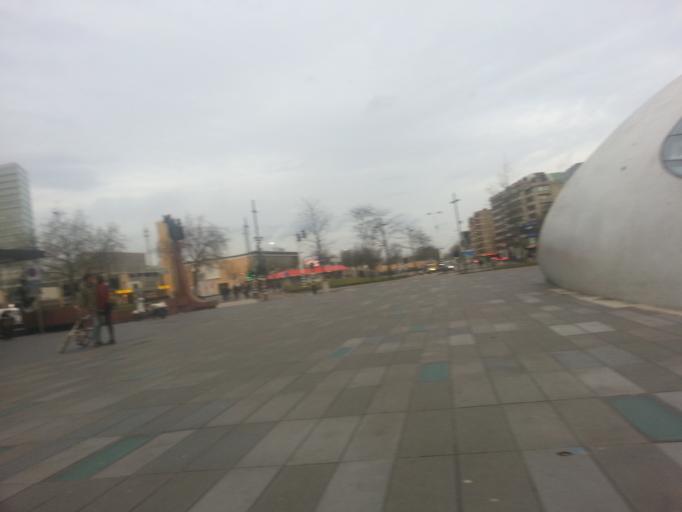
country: NL
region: North Brabant
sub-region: Gemeente Eindhoven
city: Eindhoven
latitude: 51.4413
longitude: 5.4774
